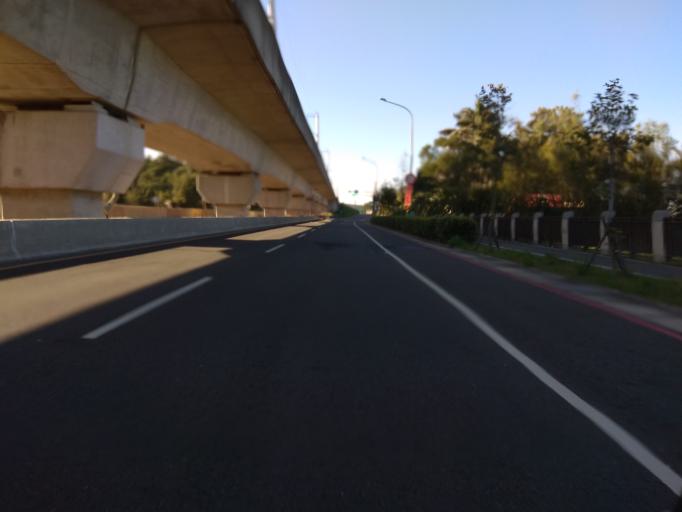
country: TW
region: Taiwan
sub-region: Hsinchu
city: Zhubei
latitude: 24.8942
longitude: 121.0774
